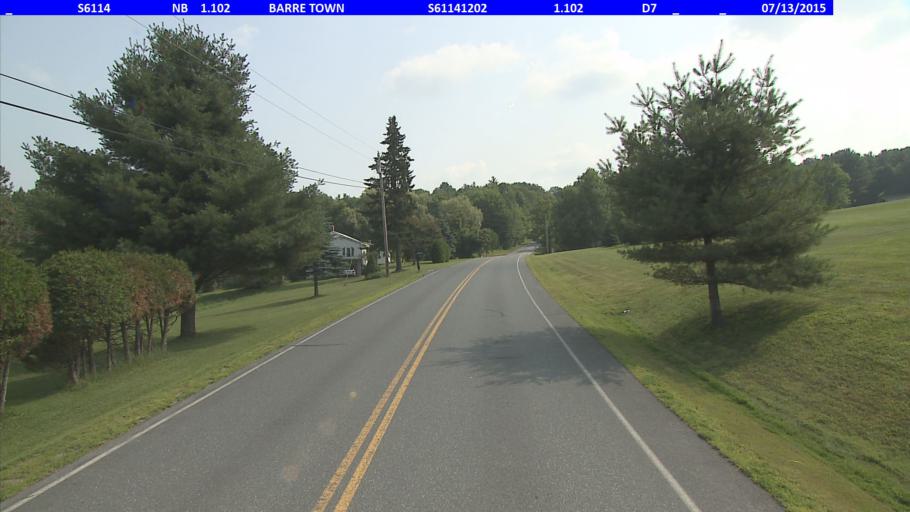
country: US
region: Vermont
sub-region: Washington County
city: Barre
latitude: 44.2059
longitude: -72.4730
